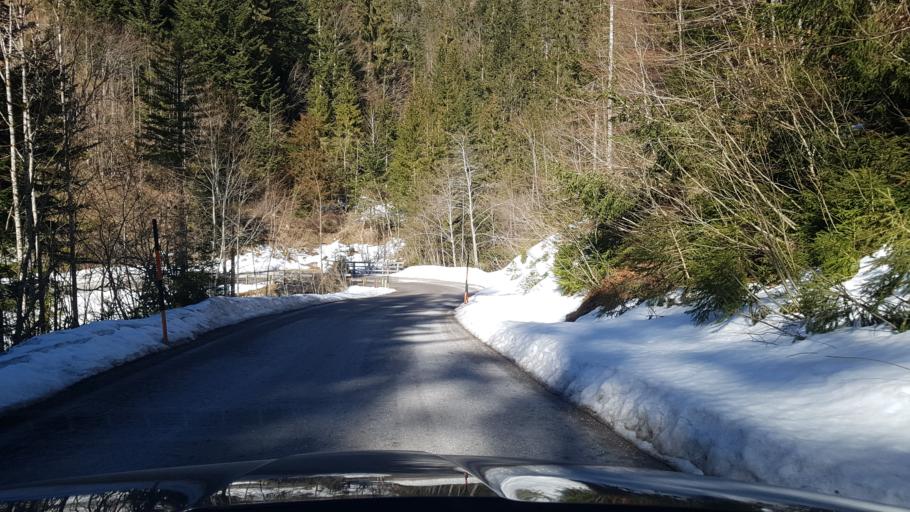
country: AT
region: Salzburg
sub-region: Politischer Bezirk Hallein
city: Abtenau
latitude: 47.6046
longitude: 13.3640
